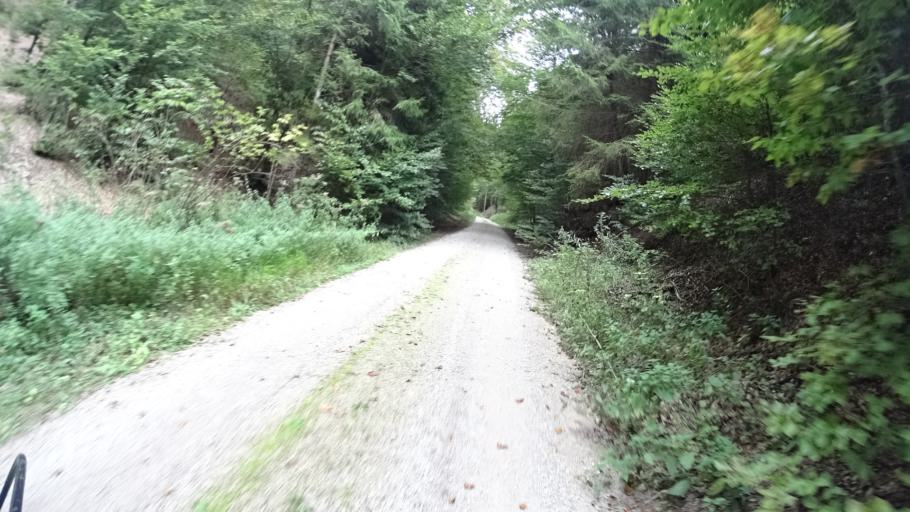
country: DE
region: Bavaria
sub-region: Upper Bavaria
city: Walting
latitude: 48.8982
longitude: 11.3043
